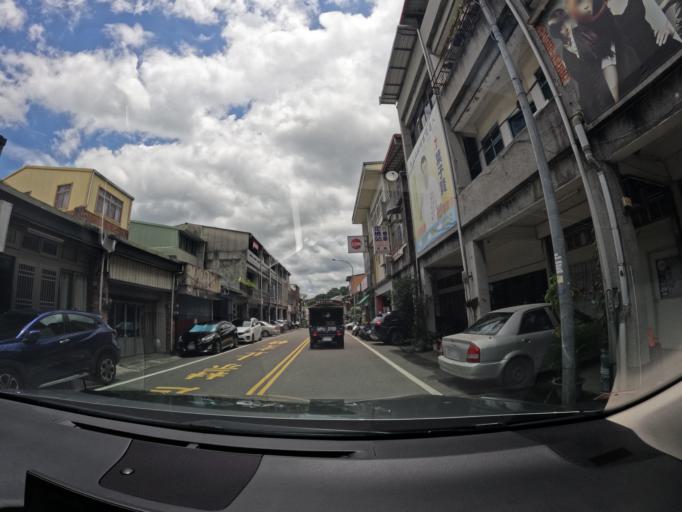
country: TW
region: Taiwan
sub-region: Miaoli
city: Miaoli
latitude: 24.6008
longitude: 120.9989
